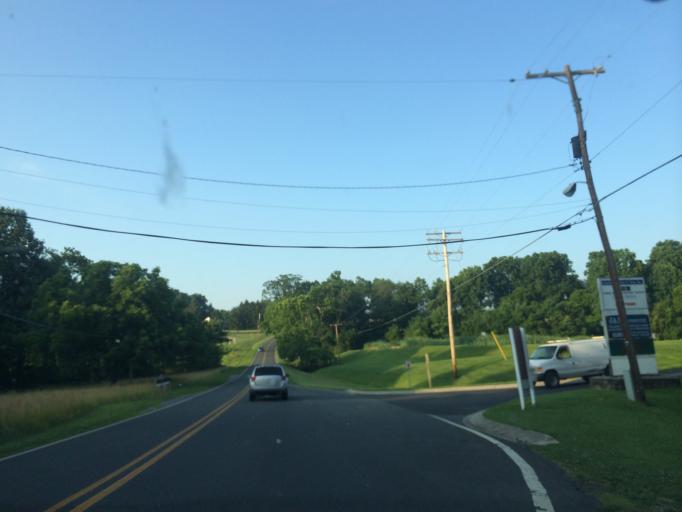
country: US
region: Maryland
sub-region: Carroll County
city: Eldersburg
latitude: 39.4321
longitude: -76.9924
